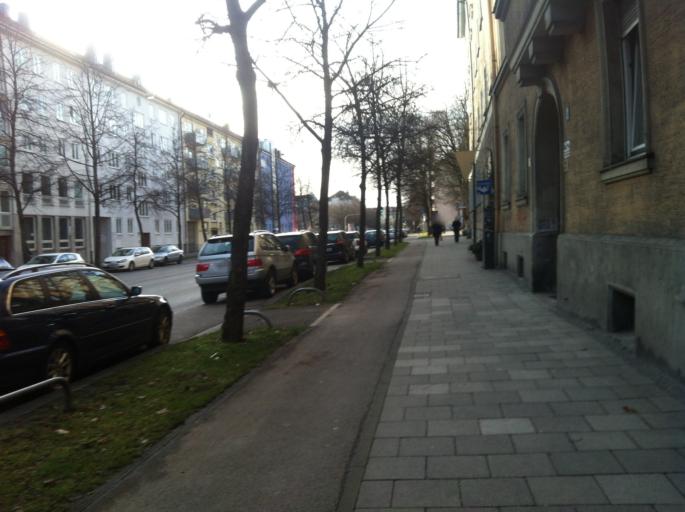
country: DE
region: Bavaria
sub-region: Upper Bavaria
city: Munich
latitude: 48.1169
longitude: 11.5484
